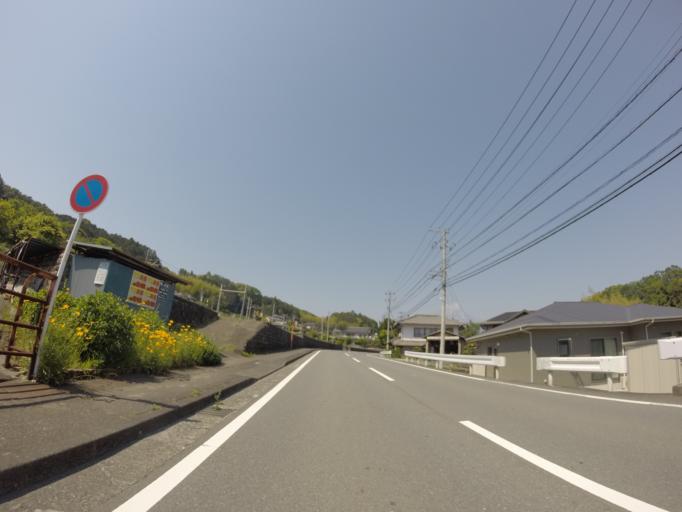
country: JP
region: Shizuoka
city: Fujinomiya
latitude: 35.2140
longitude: 138.5877
